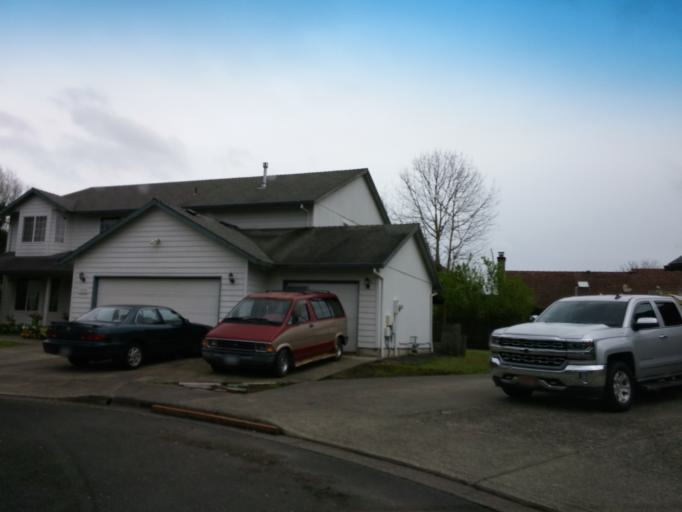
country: US
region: Oregon
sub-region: Washington County
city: Oak Hills
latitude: 45.5306
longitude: -122.8555
